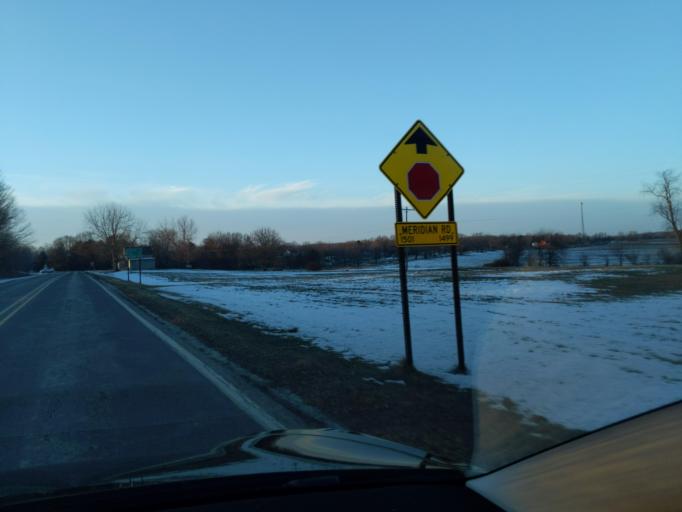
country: US
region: Michigan
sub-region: Ingham County
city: Mason
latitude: 42.5404
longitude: -84.3546
